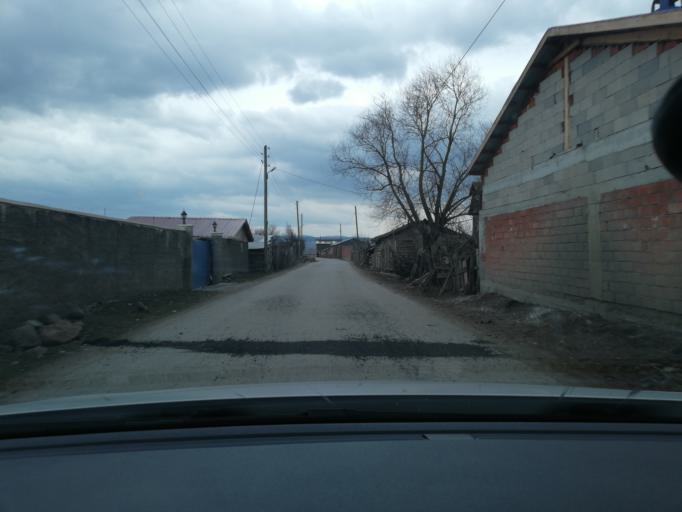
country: TR
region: Bolu
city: Gerede
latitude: 40.7330
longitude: 32.2151
